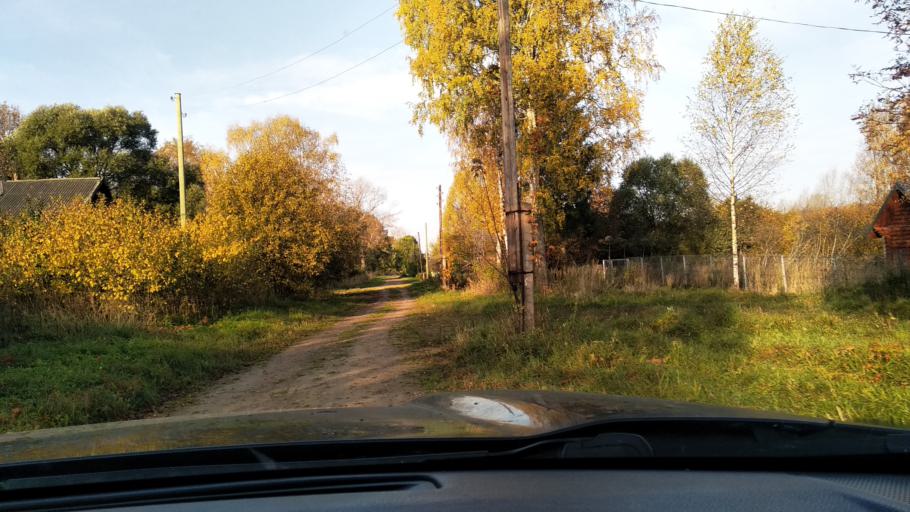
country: RU
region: Tverskaya
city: Krasnyy Kholm
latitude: 58.0093
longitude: 37.1946
